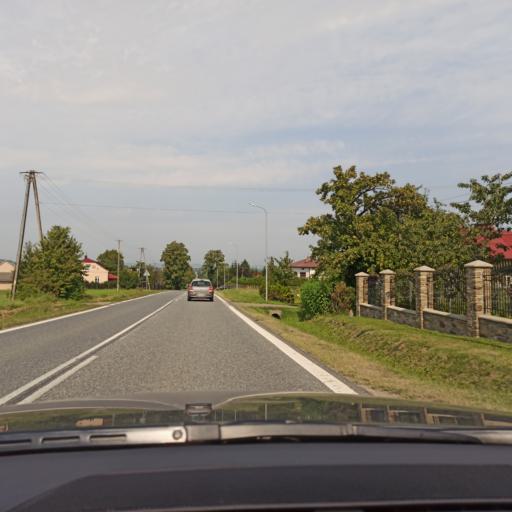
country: PL
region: Subcarpathian Voivodeship
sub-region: Powiat jasielski
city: Nowy Zmigrod
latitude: 49.5873
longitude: 21.5451
